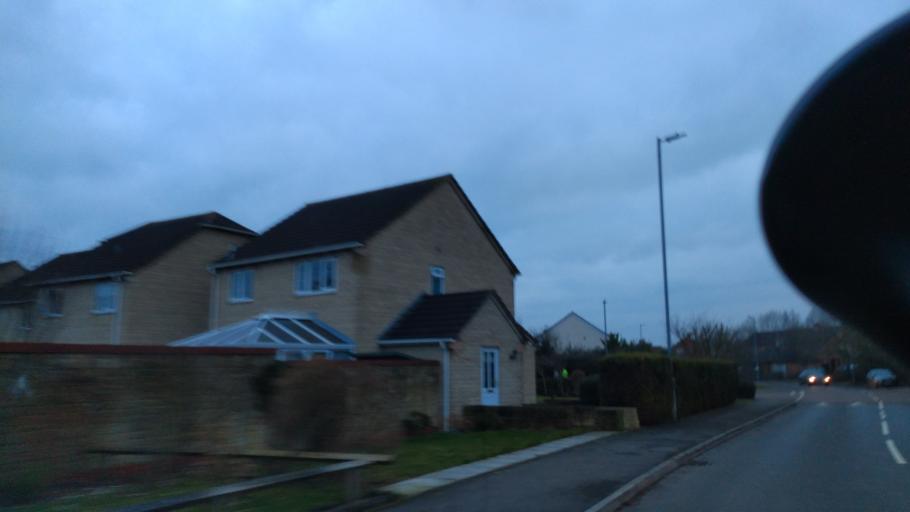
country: GB
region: England
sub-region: Wiltshire
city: Chippenham
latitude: 51.4517
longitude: -2.1460
